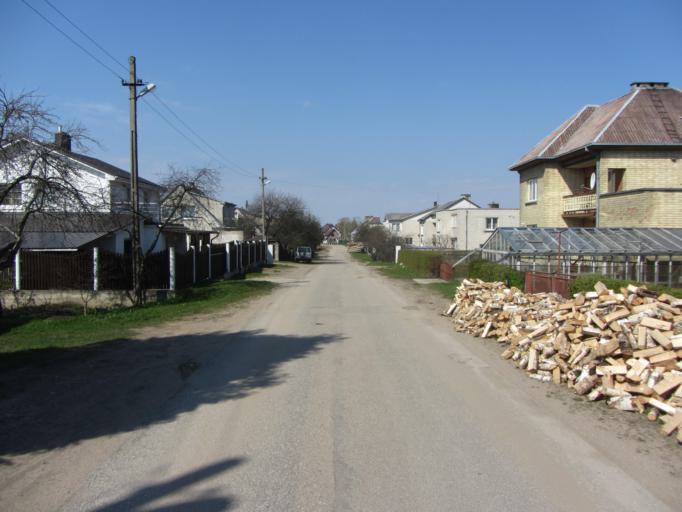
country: LT
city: Lentvaris
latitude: 54.6414
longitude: 25.0338
